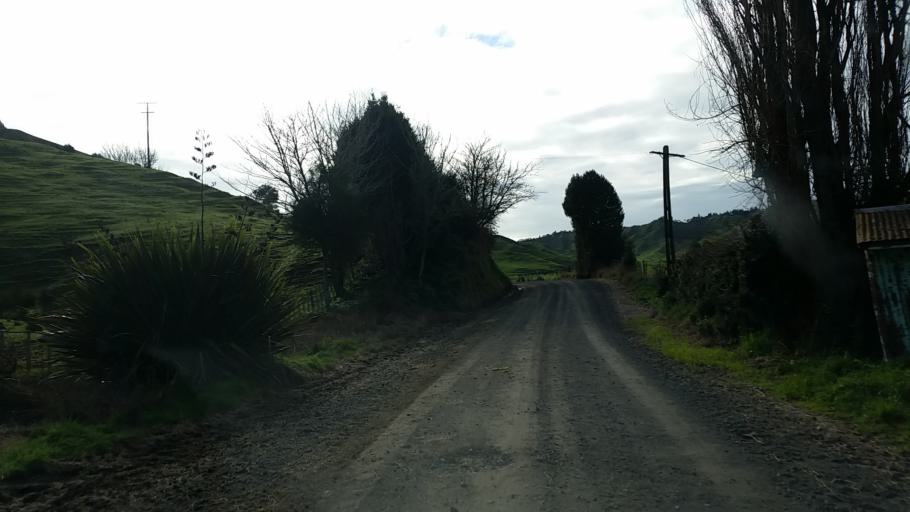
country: NZ
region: Taranaki
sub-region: South Taranaki District
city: Eltham
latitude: -39.2532
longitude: 174.5321
